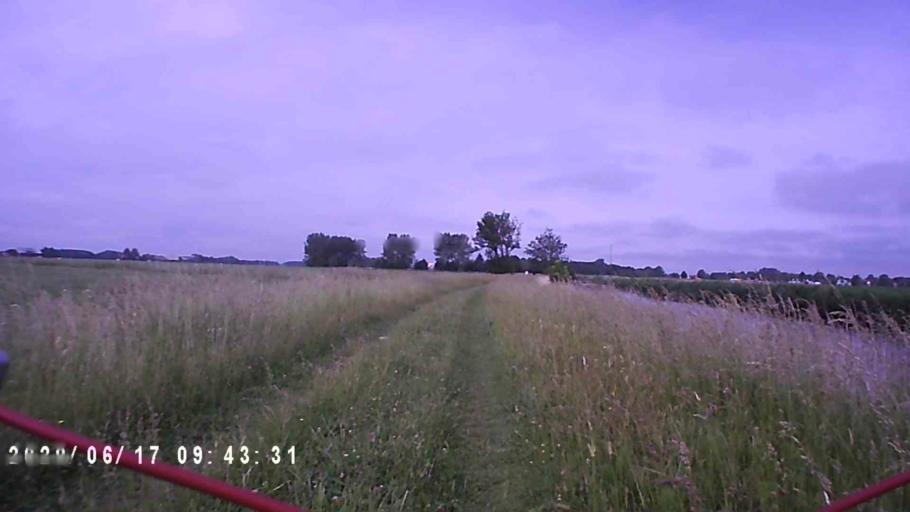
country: NL
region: Groningen
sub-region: Gemeente De Marne
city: Ulrum
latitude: 53.3521
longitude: 6.3481
